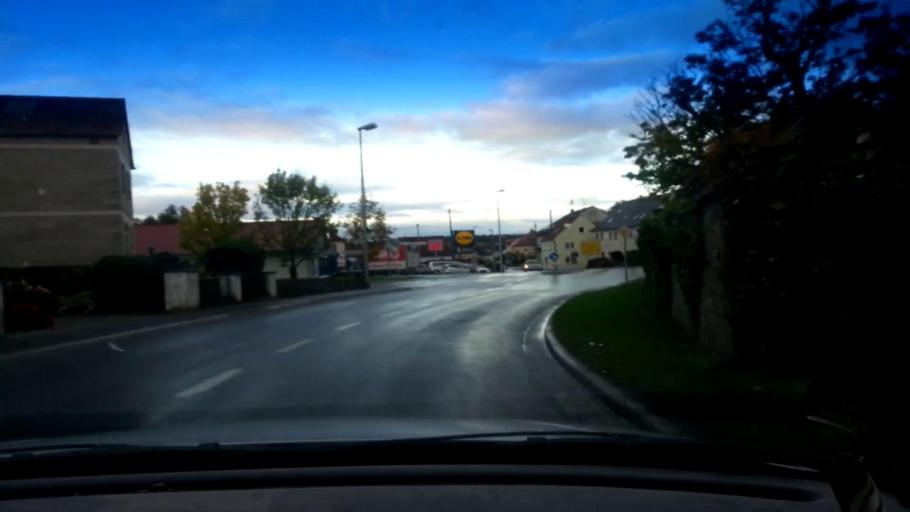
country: DE
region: Bavaria
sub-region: Upper Franconia
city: Burgebrach
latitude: 49.8255
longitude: 10.7380
